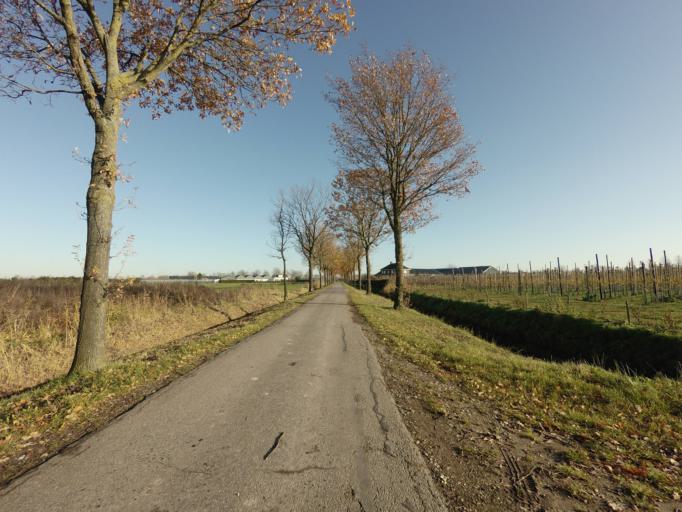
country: NL
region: Gelderland
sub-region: Gemeente Neerijnen
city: Neerijnen
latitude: 51.7905
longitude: 5.3075
